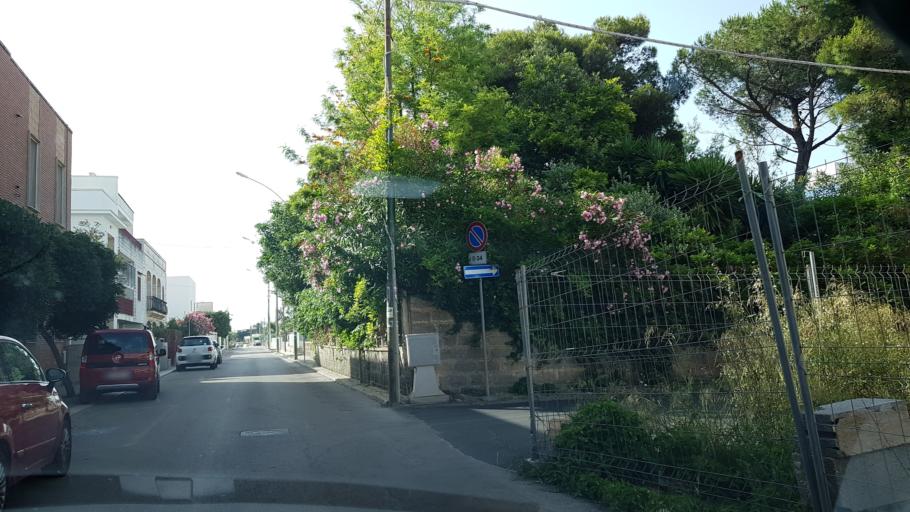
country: IT
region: Apulia
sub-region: Provincia di Lecce
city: Porto Cesareo
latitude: 40.2632
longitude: 17.8884
